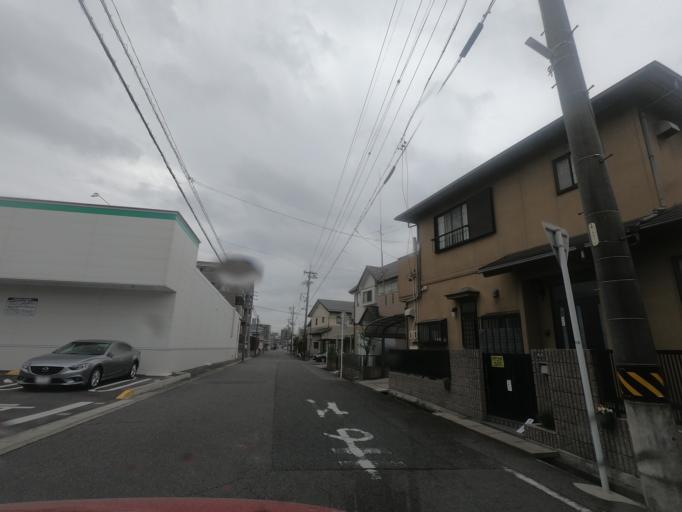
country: JP
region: Aichi
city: Kasugai
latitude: 35.2523
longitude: 136.9787
